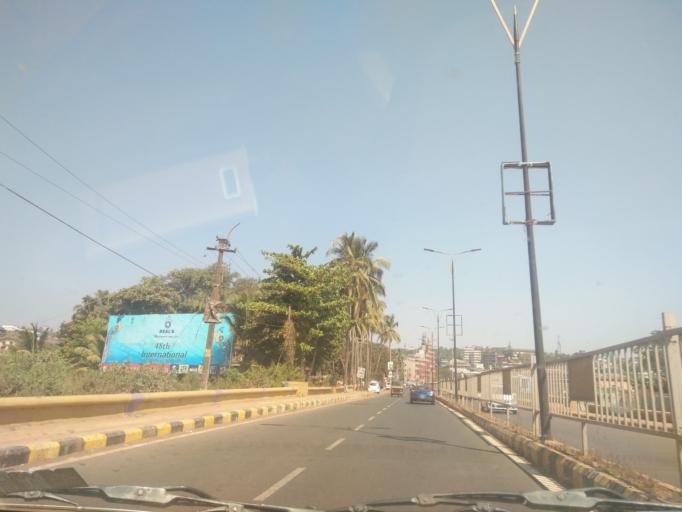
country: IN
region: Goa
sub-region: North Goa
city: Mapuca
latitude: 15.5868
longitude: 73.8083
